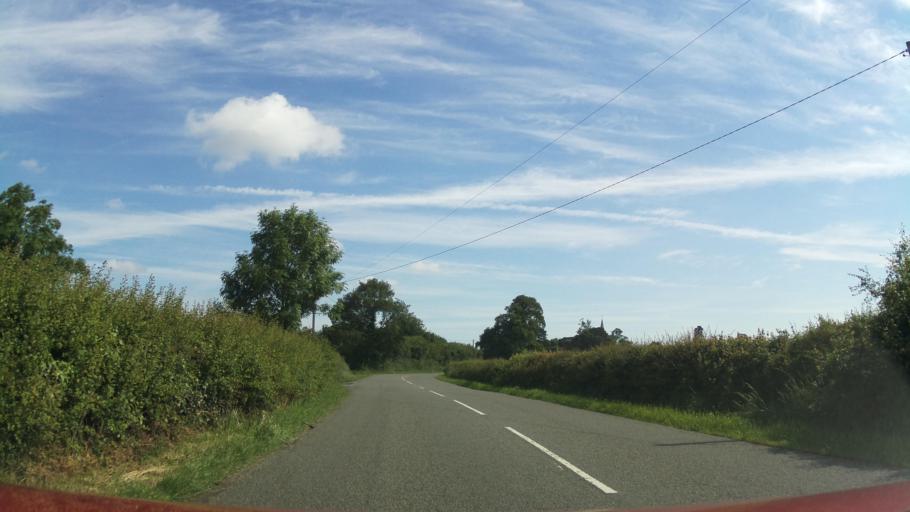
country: GB
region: England
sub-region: Lincolnshire
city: Skellingthorpe
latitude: 53.1492
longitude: -0.6312
